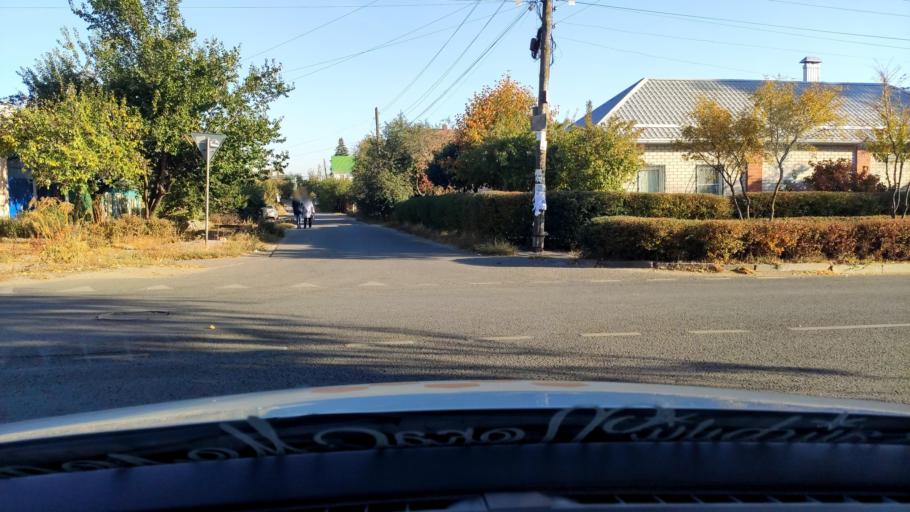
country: RU
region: Voronezj
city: Voronezh
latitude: 51.6444
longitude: 39.1726
